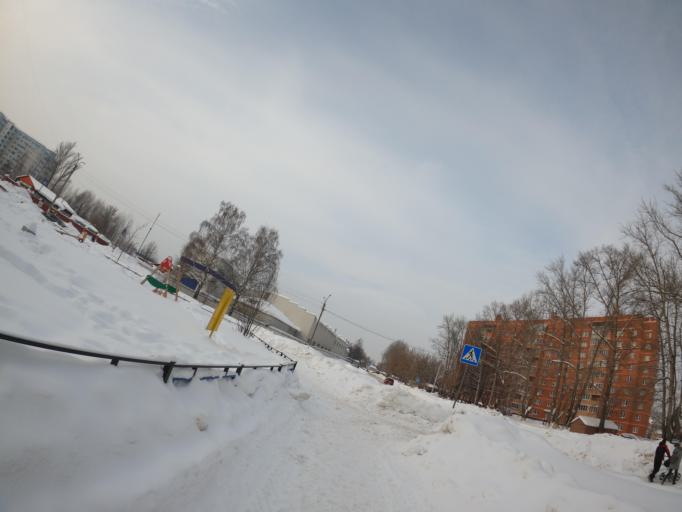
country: RU
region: Moskovskaya
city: Elektrogorsk
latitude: 55.8876
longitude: 38.7750
